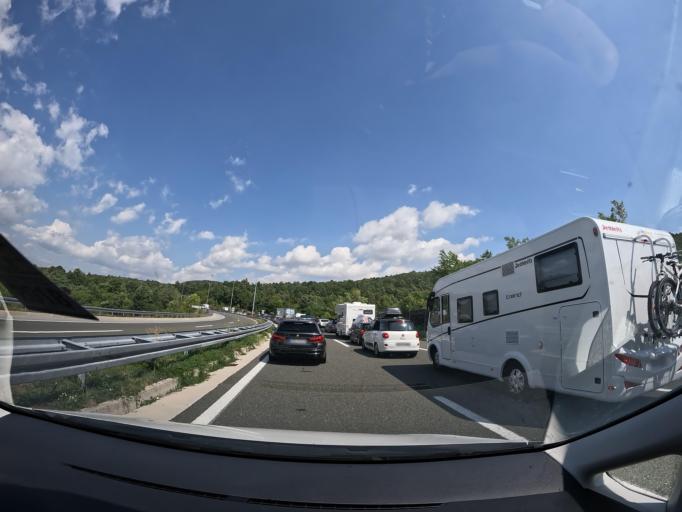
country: SI
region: Ilirska Bistrica
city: Ilirska Bistrica
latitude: 45.4882
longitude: 14.2854
